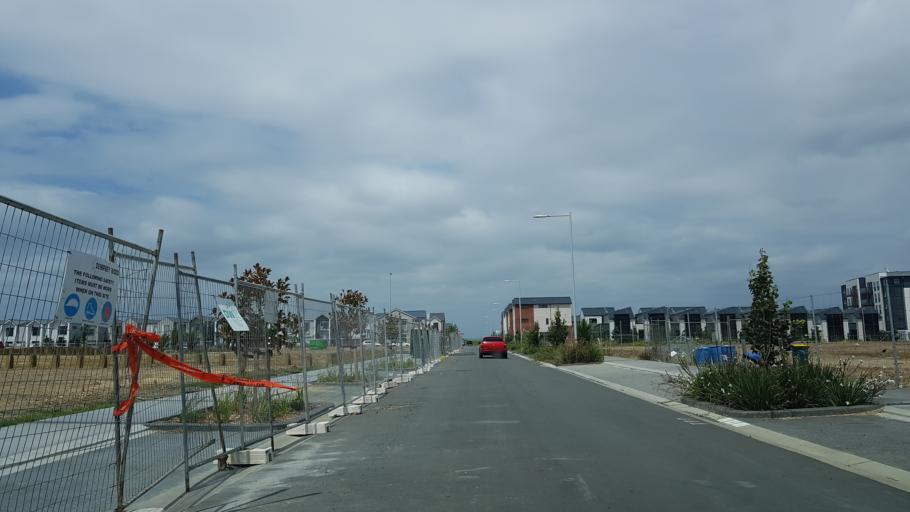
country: NZ
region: Auckland
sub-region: Auckland
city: Rosebank
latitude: -36.7903
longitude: 174.6645
